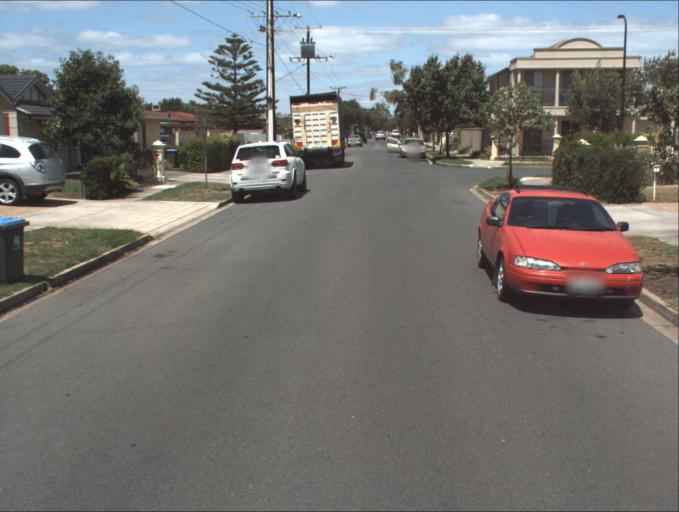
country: AU
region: South Australia
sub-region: Charles Sturt
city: Woodville North
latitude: -34.8596
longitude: 138.5640
